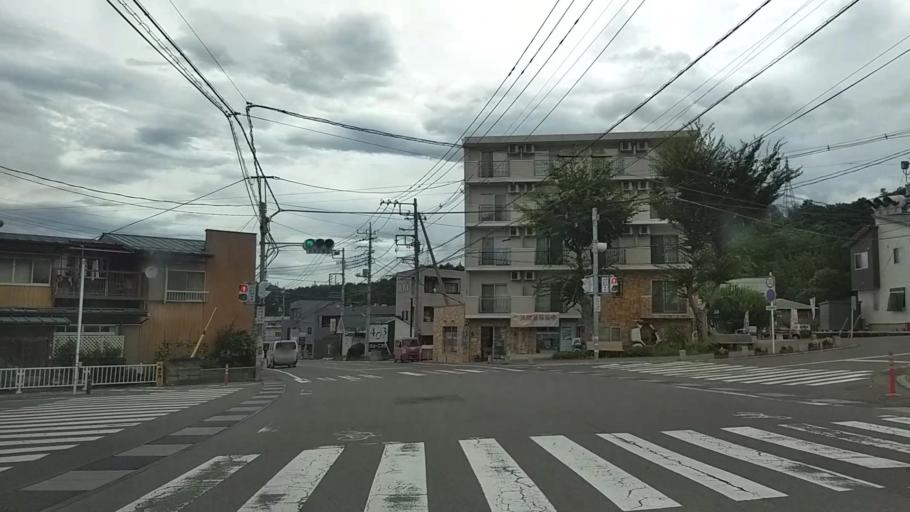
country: JP
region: Yamanashi
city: Otsuki
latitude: 35.5403
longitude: 138.8965
